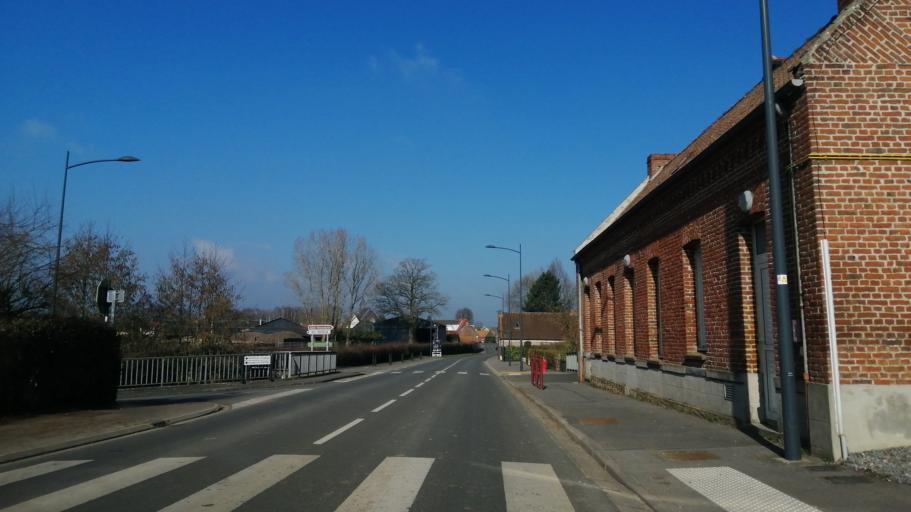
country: FR
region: Nord-Pas-de-Calais
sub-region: Departement du Pas-de-Calais
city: Ranchicourt
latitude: 50.4136
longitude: 2.5837
